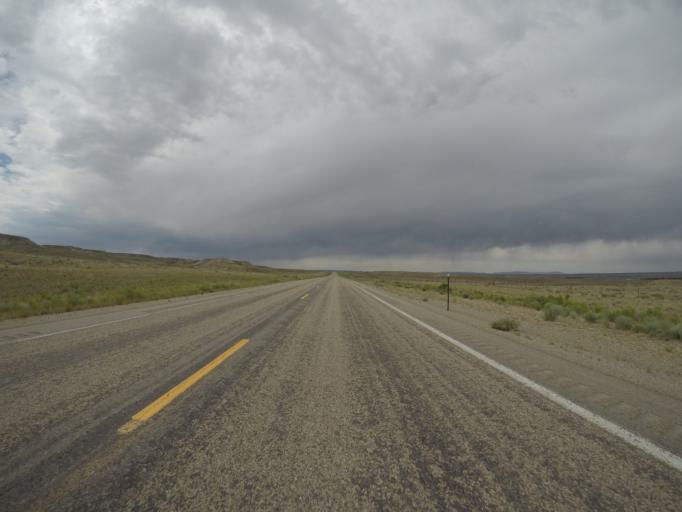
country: US
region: Wyoming
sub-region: Lincoln County
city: Kemmerer
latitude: 41.9517
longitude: -110.0231
